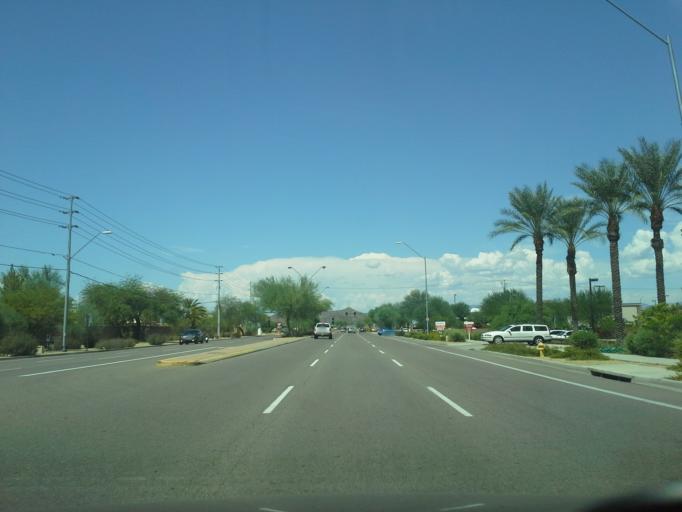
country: US
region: Arizona
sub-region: Maricopa County
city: Paradise Valley
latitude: 33.6749
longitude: -112.0310
